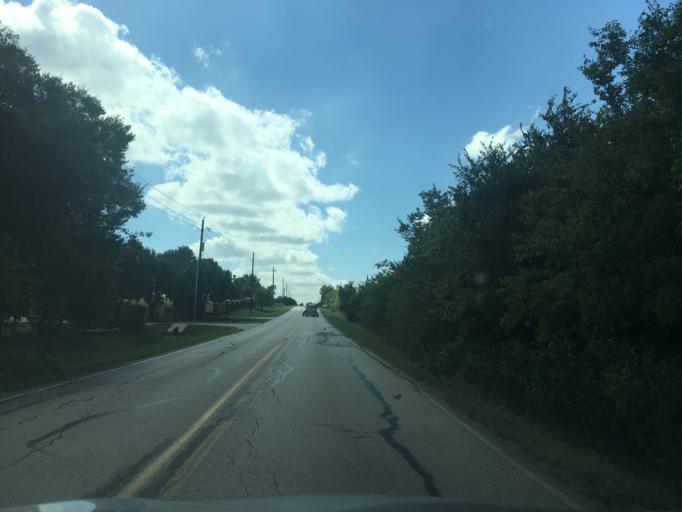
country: US
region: Texas
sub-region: Dallas County
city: Sachse
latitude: 32.9625
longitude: -96.5705
